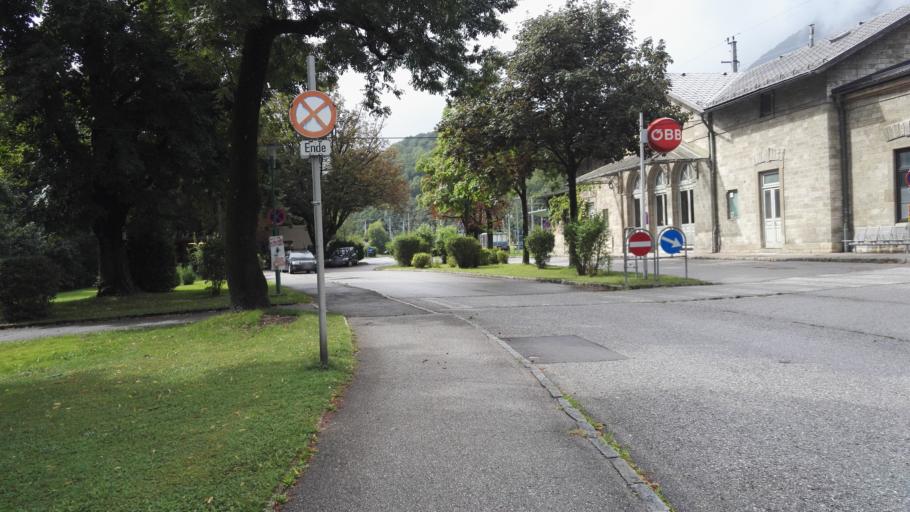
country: AT
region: Lower Austria
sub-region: Politischer Bezirk Neunkirchen
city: Payerbach
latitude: 47.6956
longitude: 15.8638
